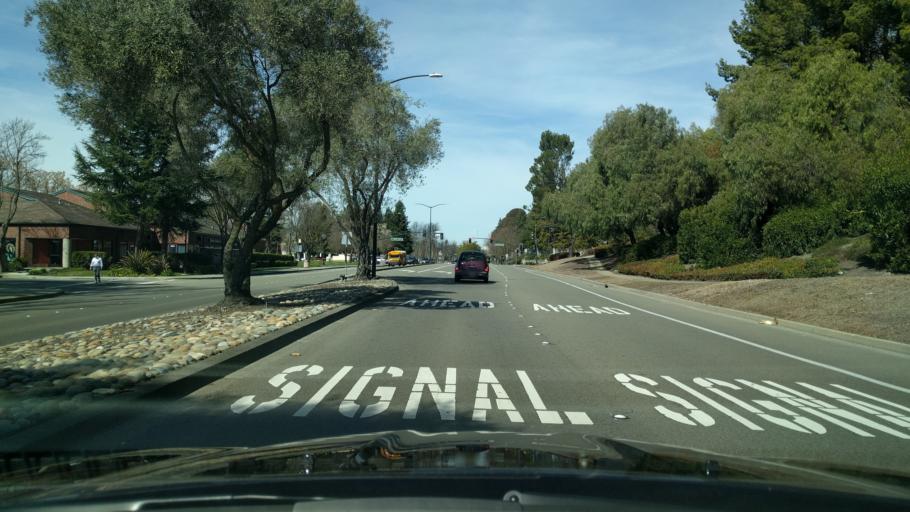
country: US
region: California
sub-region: Contra Costa County
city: San Ramon
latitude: 37.7647
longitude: -121.9506
